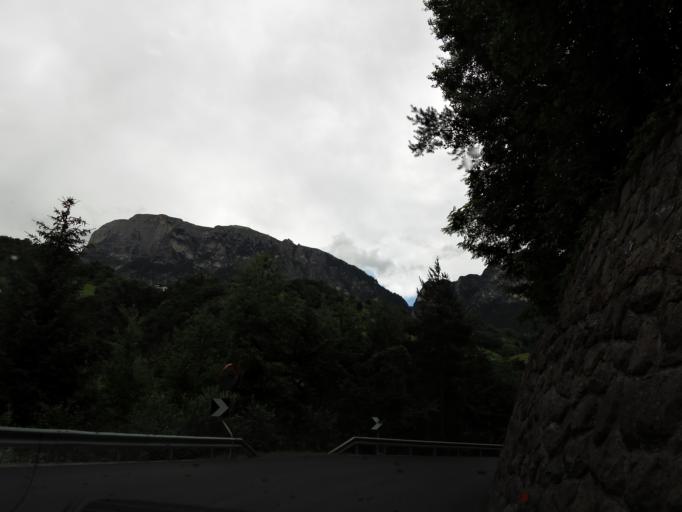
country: IT
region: Trentino-Alto Adige
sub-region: Bolzano
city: Fie Allo Sciliar
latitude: 46.5083
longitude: 11.5074
